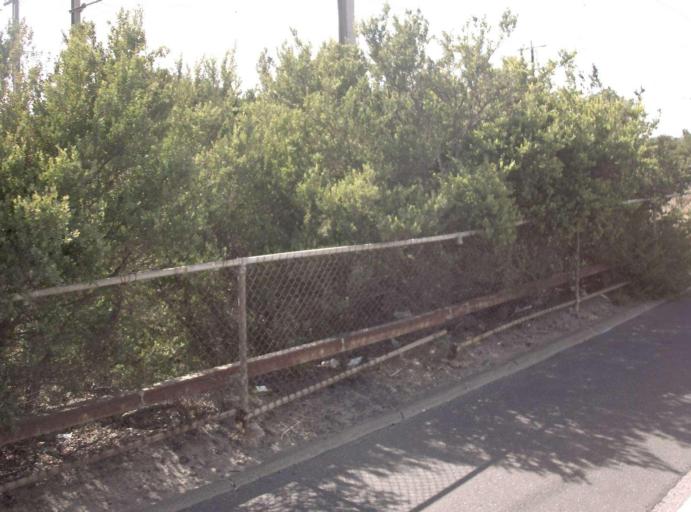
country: AU
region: Victoria
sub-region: Kingston
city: Chelsea
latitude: -38.0480
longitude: 145.1140
